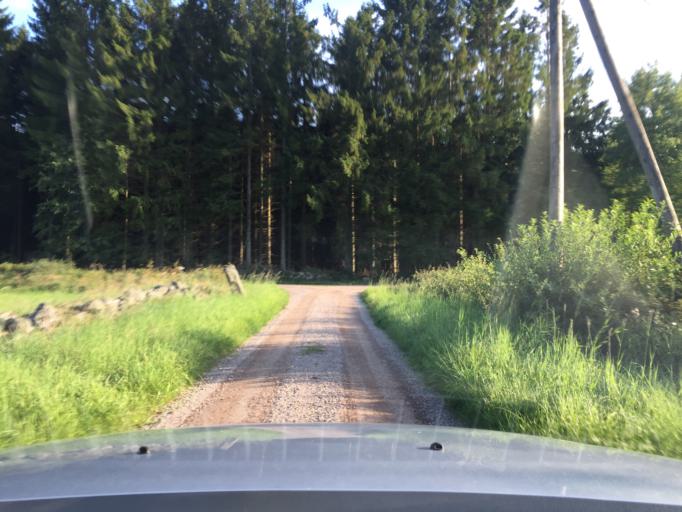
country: SE
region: Skane
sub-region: Hassleholms Kommun
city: Sosdala
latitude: 56.0219
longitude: 13.7045
